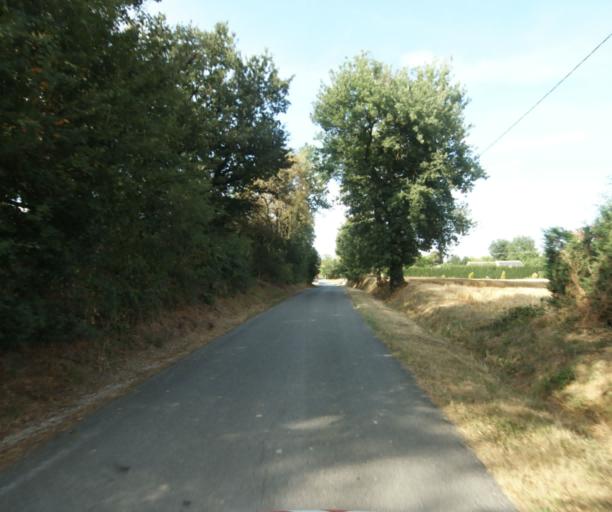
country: FR
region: Midi-Pyrenees
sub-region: Departement de la Haute-Garonne
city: Revel
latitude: 43.5021
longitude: 1.9960
